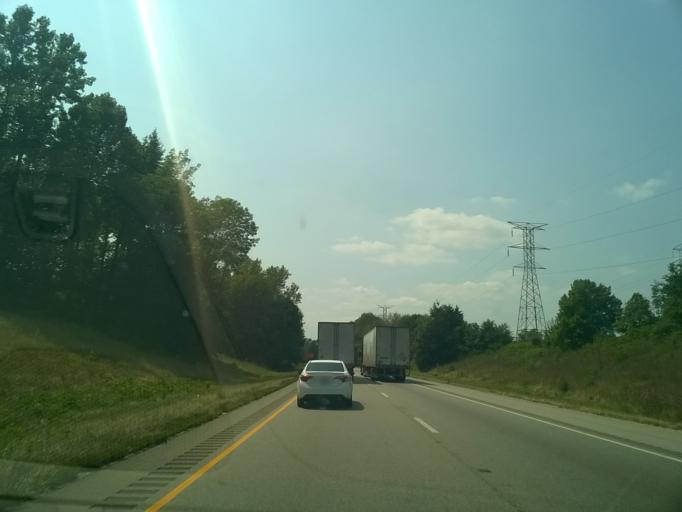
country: US
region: Indiana
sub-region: Vigo County
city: Seelyville
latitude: 39.4421
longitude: -87.2752
